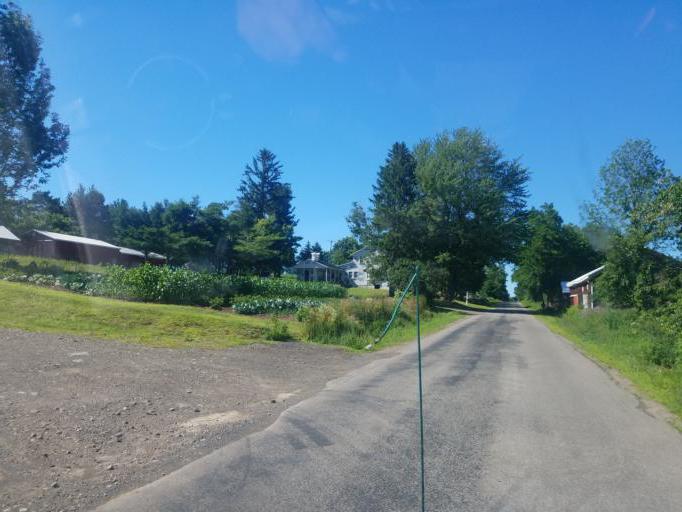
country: US
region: New York
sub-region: Wayne County
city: Lyons
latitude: 43.1210
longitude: -77.0385
